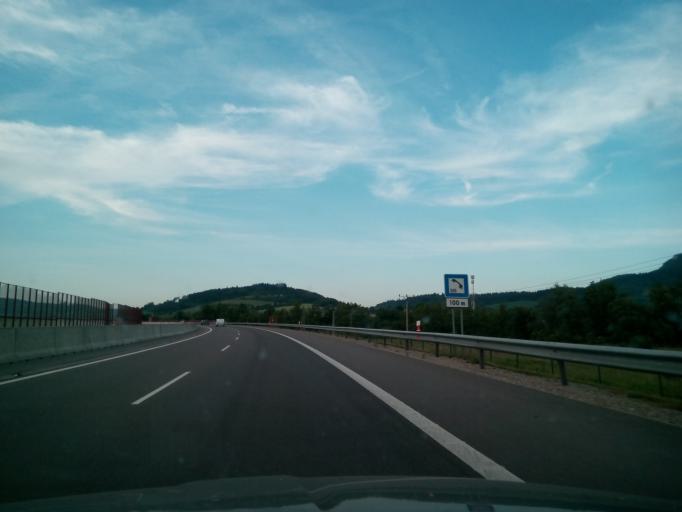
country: SK
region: Trenciansky
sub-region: Okres Povazska Bystrica
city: Povazska Bystrica
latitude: 49.1365
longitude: 18.4615
